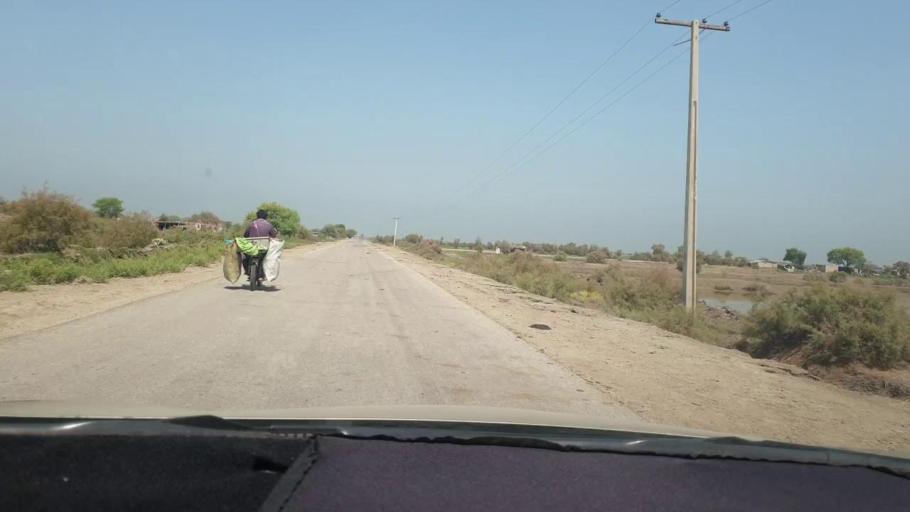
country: PK
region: Sindh
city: Miro Khan
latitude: 27.8252
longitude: 68.0197
